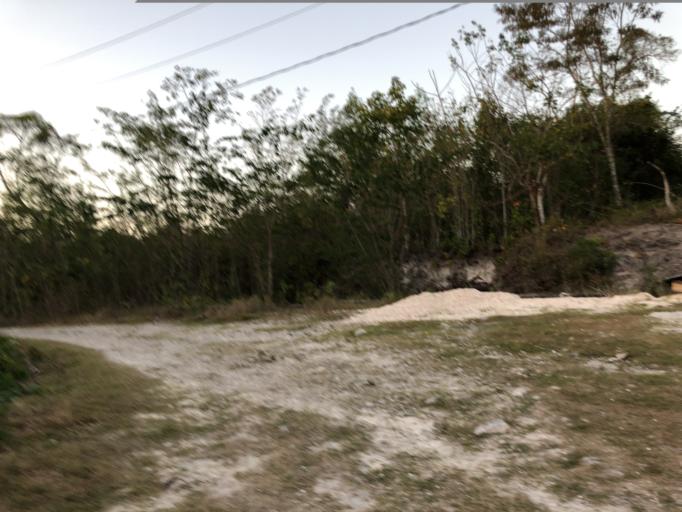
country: MX
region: Quintana Roo
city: Nicolas Bravo
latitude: 18.4536
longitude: -89.3042
